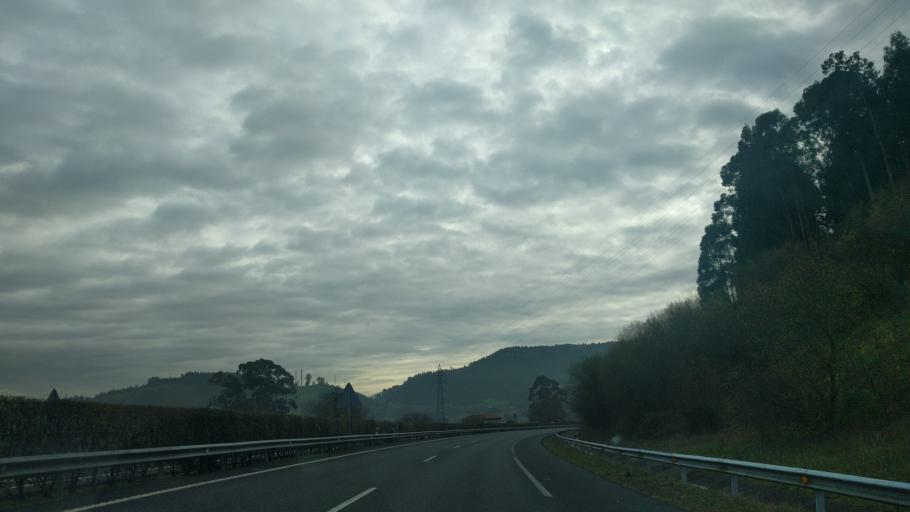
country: ES
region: Cantabria
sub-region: Provincia de Cantabria
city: Barcena de Cicero
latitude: 43.4115
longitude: -3.5199
